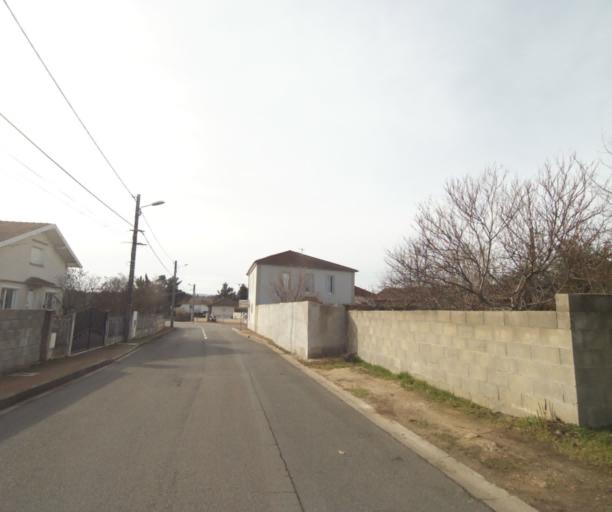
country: FR
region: Rhone-Alpes
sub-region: Departement de la Loire
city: Roanne
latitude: 46.0193
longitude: 4.0500
